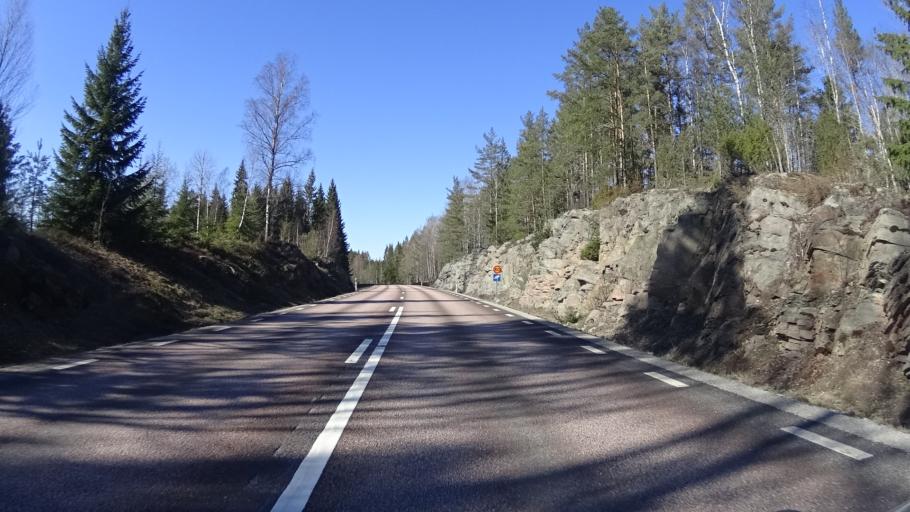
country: SE
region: Vaermland
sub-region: Karlstads Kommun
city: Edsvalla
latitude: 59.6109
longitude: 12.9879
